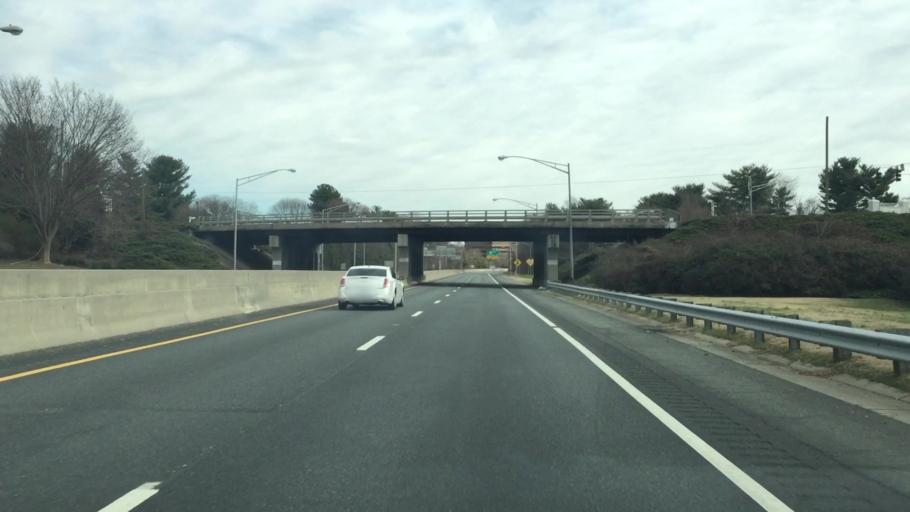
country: US
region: North Carolina
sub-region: Forsyth County
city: Winston-Salem
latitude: 36.0917
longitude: -80.2874
